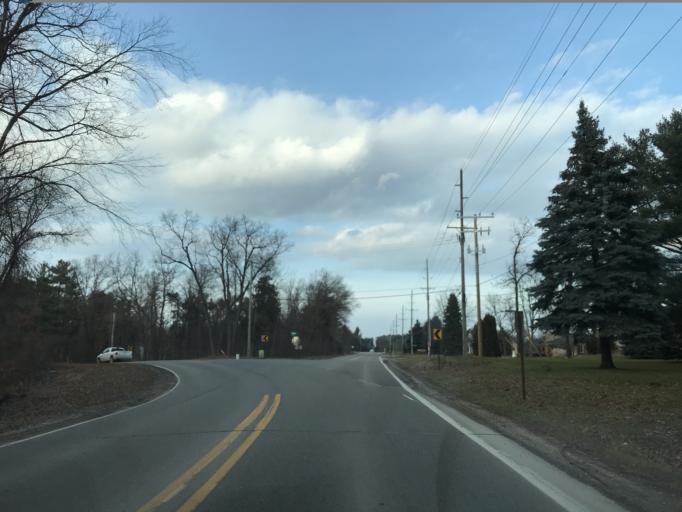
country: US
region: Michigan
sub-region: Oakland County
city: South Lyon
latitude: 42.4655
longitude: -83.6968
